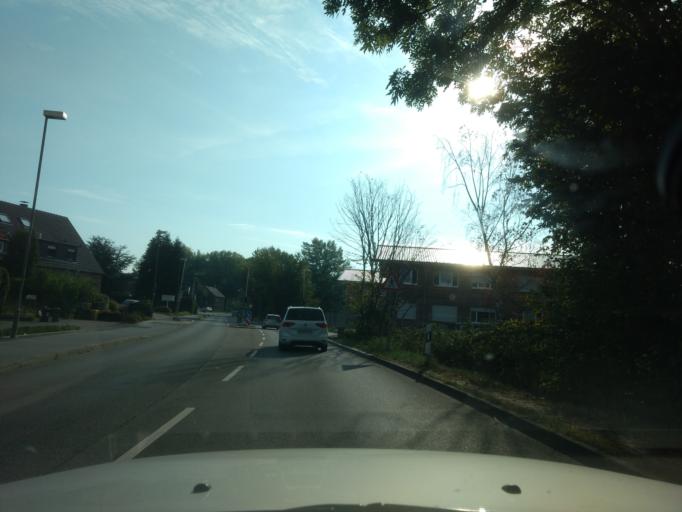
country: DE
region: North Rhine-Westphalia
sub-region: Regierungsbezirk Dusseldorf
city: Meerbusch
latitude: 51.2489
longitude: 6.7255
